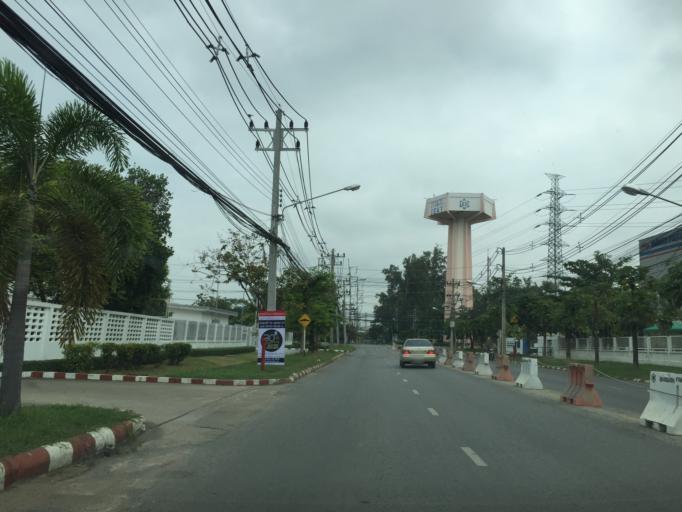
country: TH
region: Lamphun
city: Lamphun
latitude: 18.5878
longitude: 99.0511
